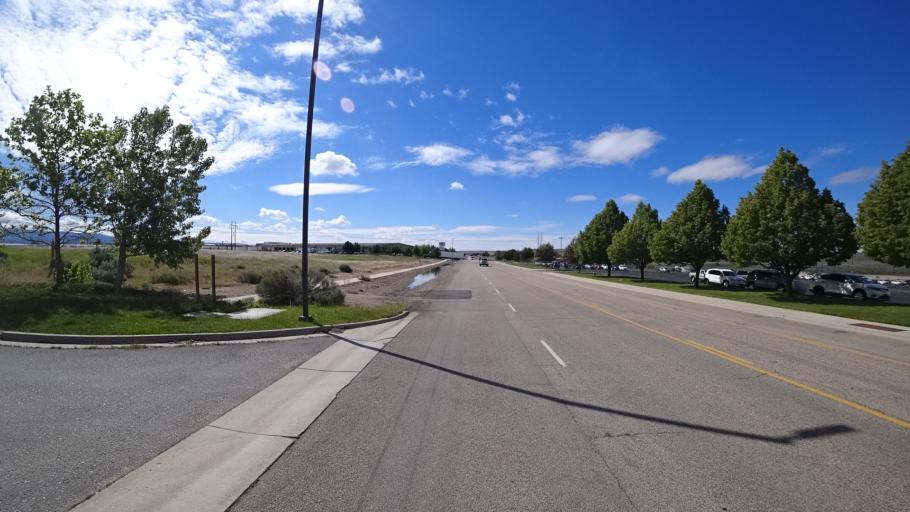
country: US
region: Idaho
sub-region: Ada County
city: Boise
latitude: 43.5361
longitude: -116.1612
